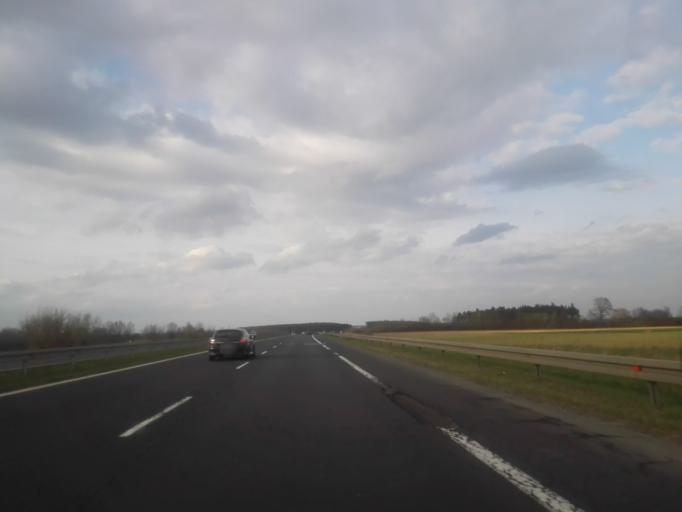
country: PL
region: Lodz Voivodeship
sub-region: Powiat piotrkowski
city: Wola Krzysztoporska
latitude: 51.2915
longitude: 19.5433
